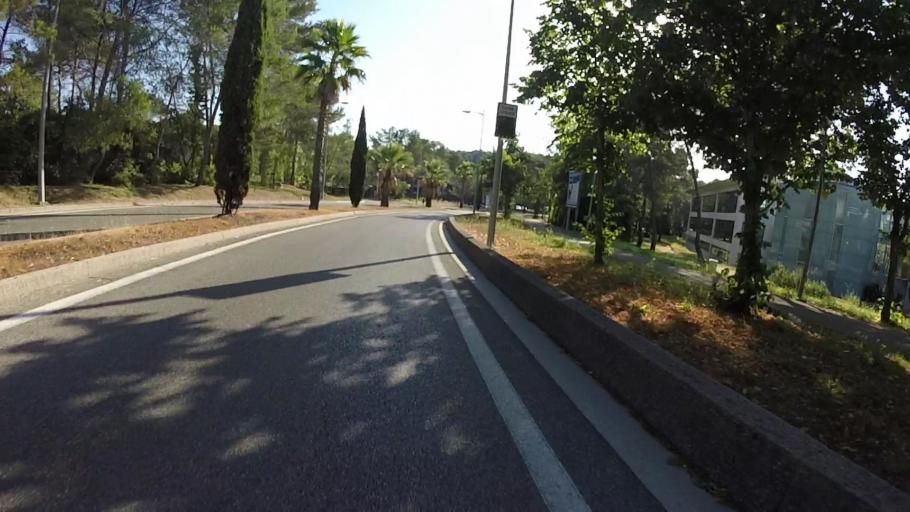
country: FR
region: Provence-Alpes-Cote d'Azur
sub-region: Departement des Alpes-Maritimes
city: Mougins
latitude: 43.6121
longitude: 7.0138
